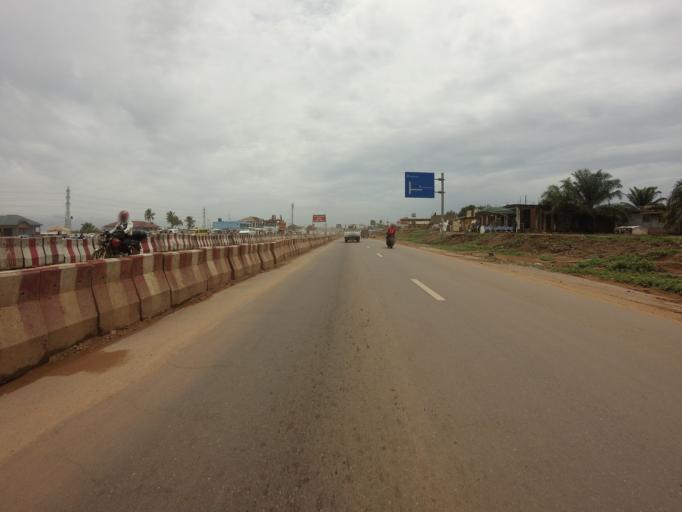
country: GH
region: Greater Accra
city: Achiaman
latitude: 5.6863
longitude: -0.2801
